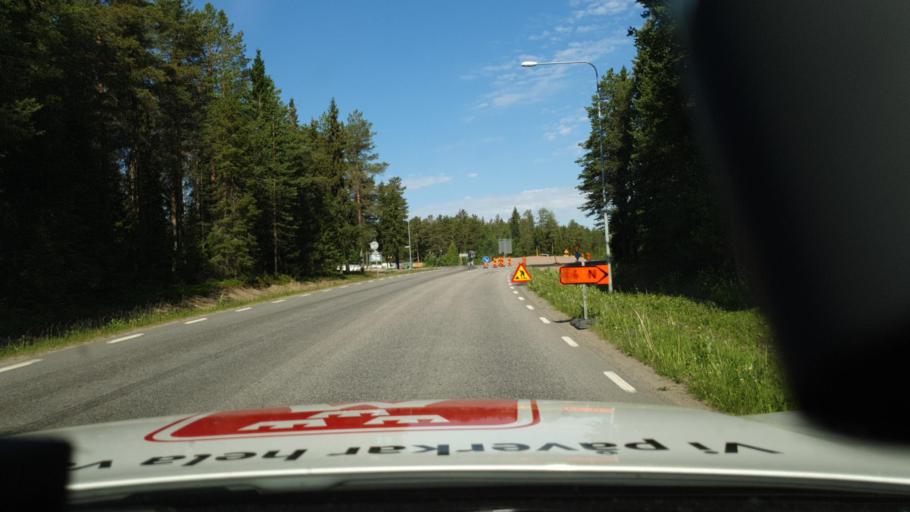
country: SE
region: Norrbotten
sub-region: Lulea Kommun
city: Ranea
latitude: 65.8632
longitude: 22.3100
